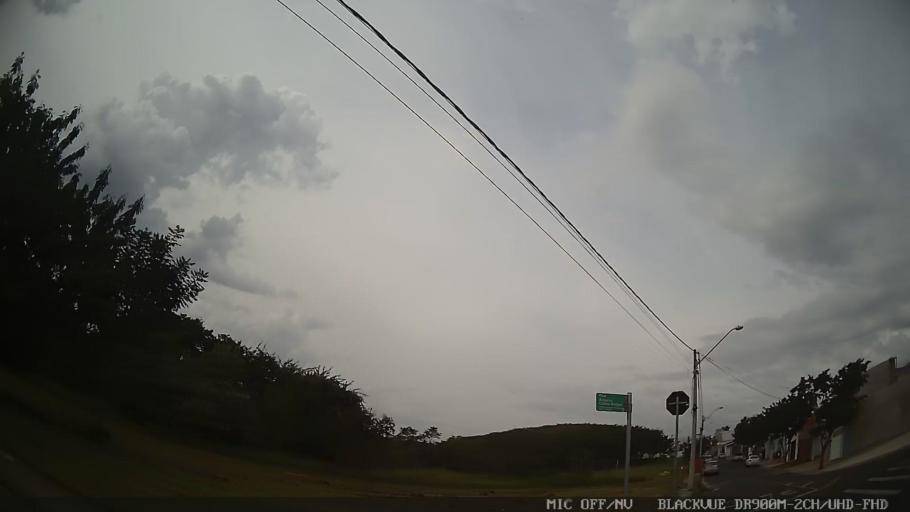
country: BR
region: Sao Paulo
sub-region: Indaiatuba
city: Indaiatuba
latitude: -23.0995
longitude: -47.2550
